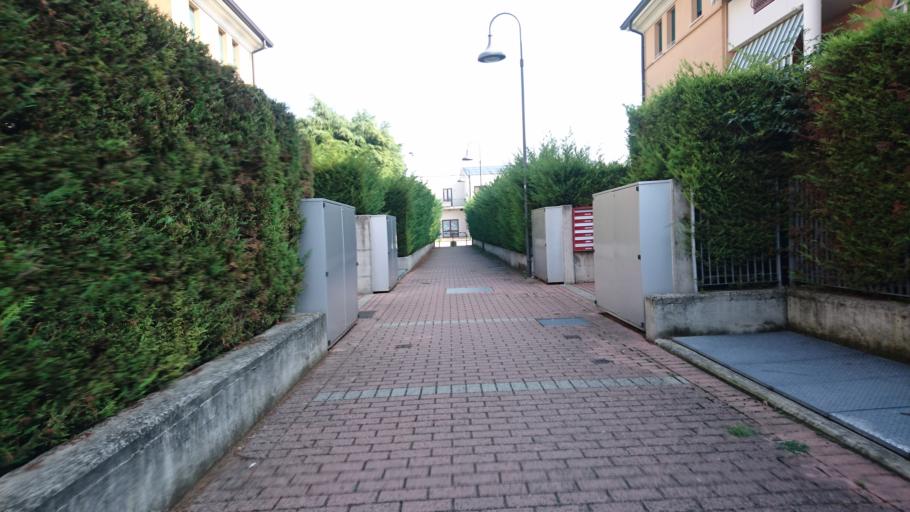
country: IT
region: Veneto
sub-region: Provincia di Padova
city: Albignasego
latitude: 45.3435
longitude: 11.8638
